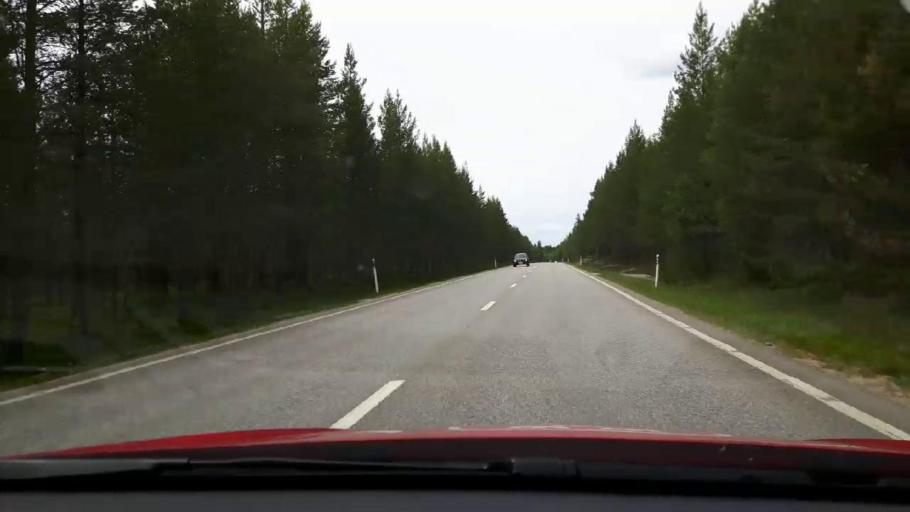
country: SE
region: Jaemtland
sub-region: Harjedalens Kommun
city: Sveg
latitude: 62.0602
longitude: 14.2884
